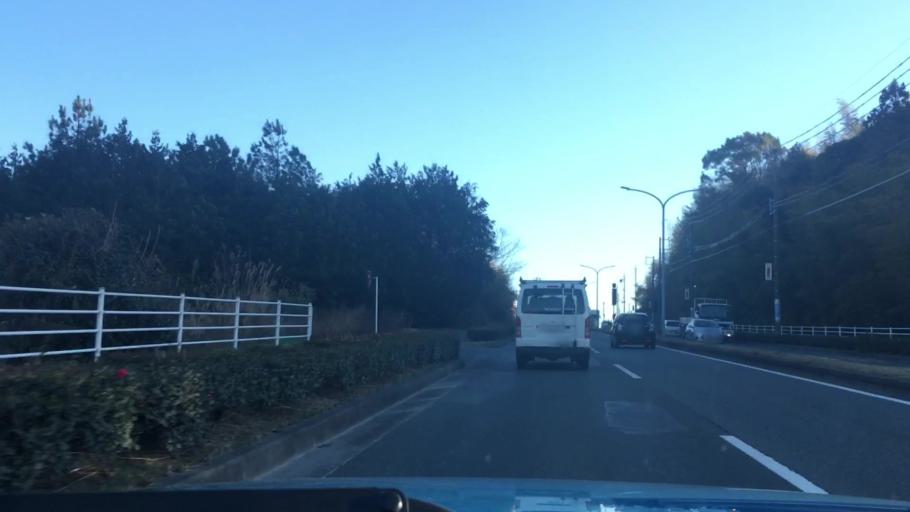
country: JP
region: Shizuoka
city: Hamamatsu
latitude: 34.7444
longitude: 137.6660
